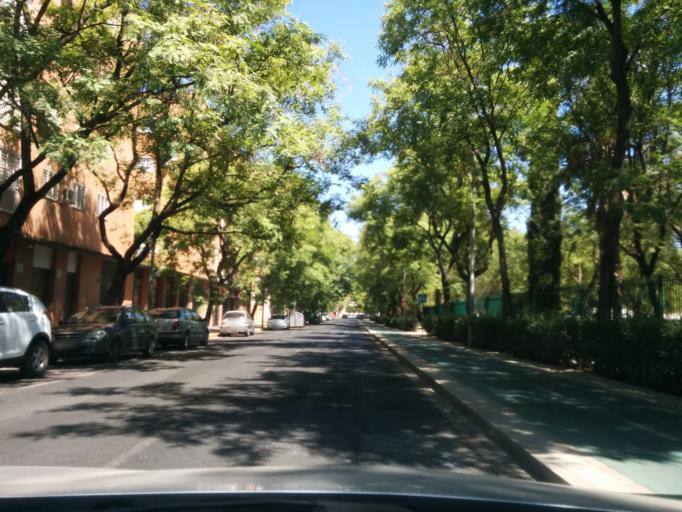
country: ES
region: Andalusia
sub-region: Provincia de Sevilla
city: Sevilla
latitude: 37.3644
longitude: -5.9746
